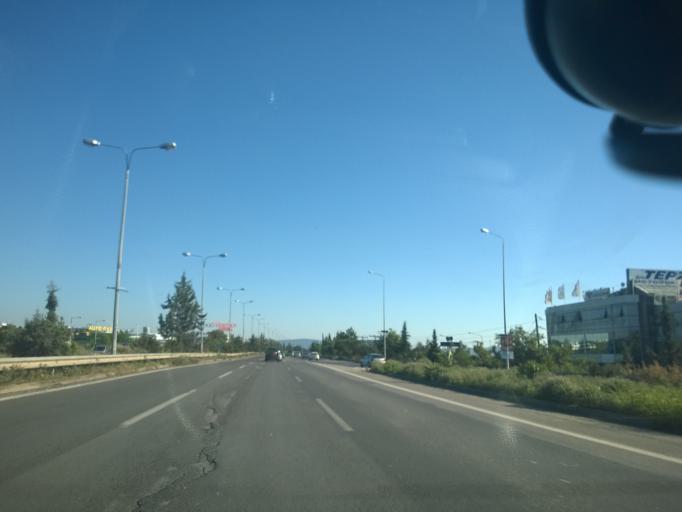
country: GR
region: Central Macedonia
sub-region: Nomos Thessalonikis
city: Pylaia
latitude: 40.5791
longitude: 22.9792
